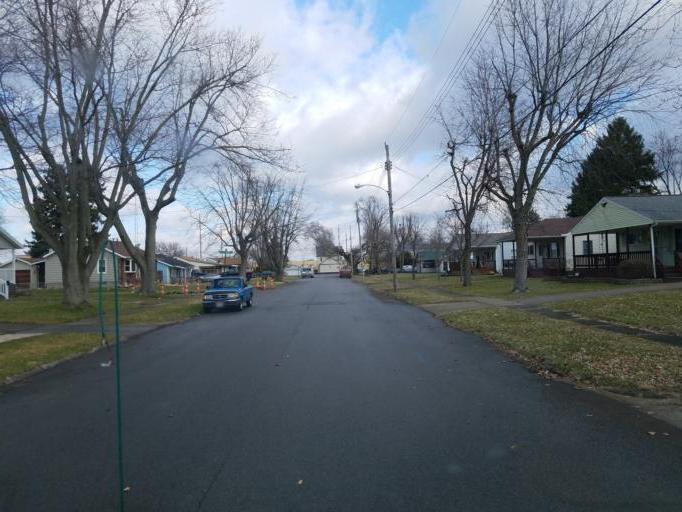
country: US
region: Ohio
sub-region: Marion County
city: Marion
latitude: 40.5845
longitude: -83.1560
